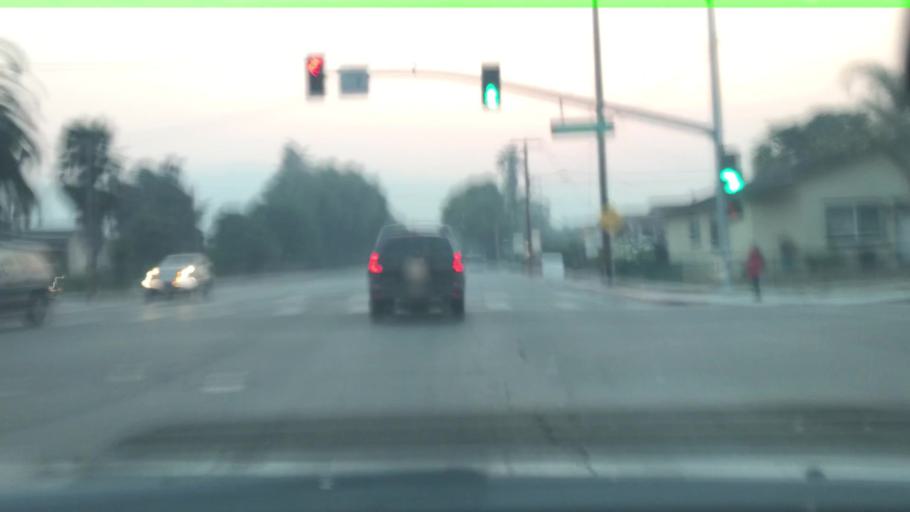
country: US
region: California
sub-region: Santa Clara County
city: Gilroy
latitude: 36.9997
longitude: -121.5680
